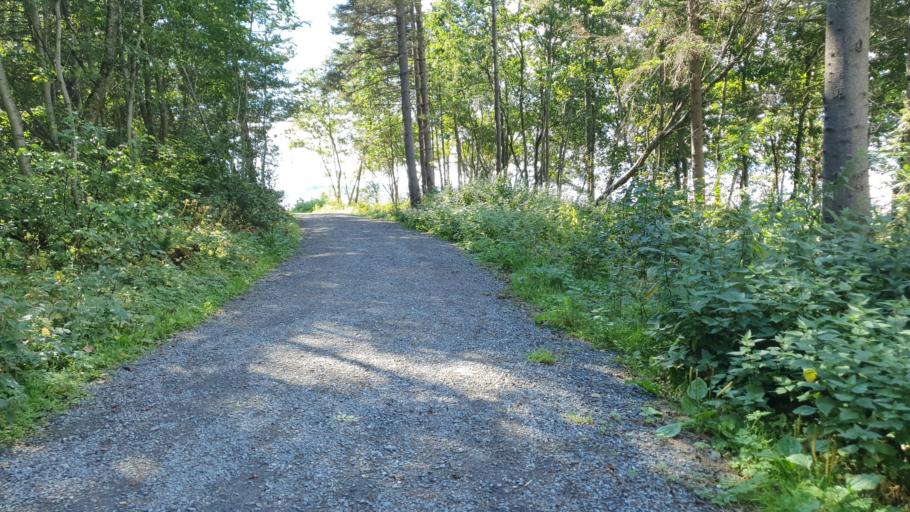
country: NO
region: Nord-Trondelag
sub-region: Levanger
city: Levanger
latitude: 63.7802
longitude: 11.3857
